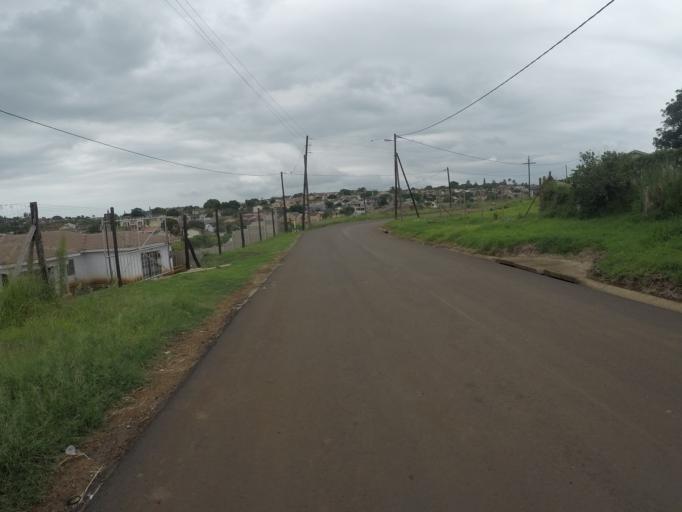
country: ZA
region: KwaZulu-Natal
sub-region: uThungulu District Municipality
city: Empangeni
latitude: -28.7756
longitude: 31.8578
